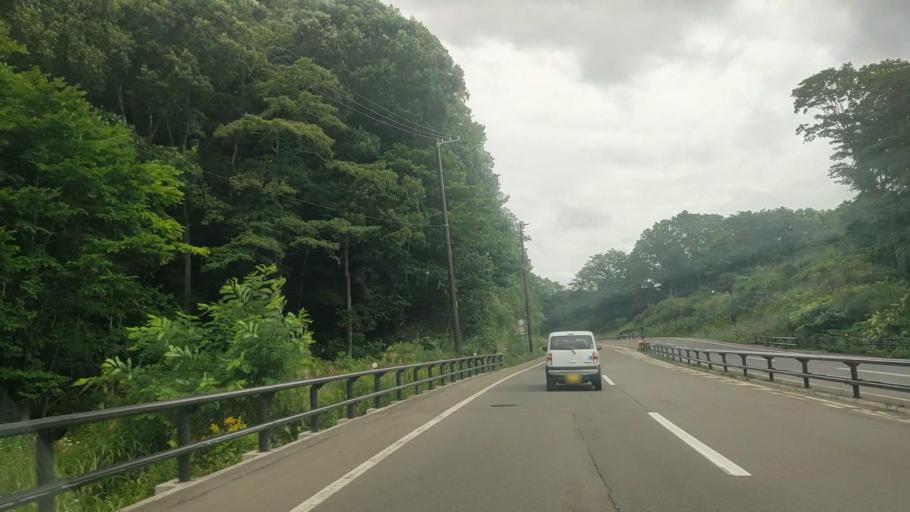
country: JP
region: Hokkaido
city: Nanae
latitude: 41.9637
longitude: 140.6482
